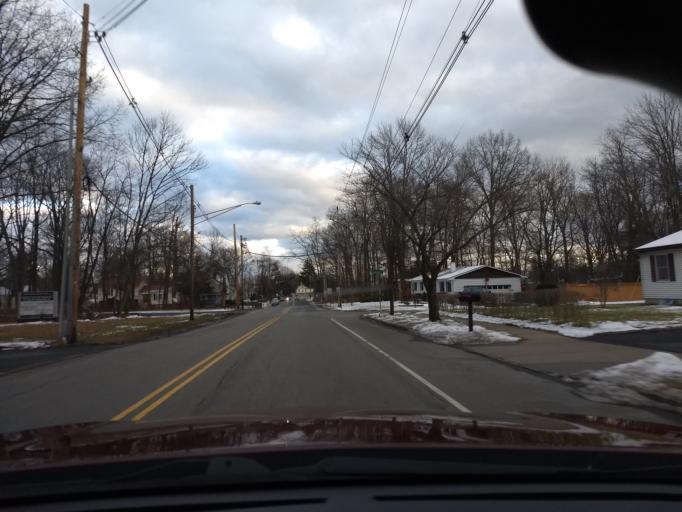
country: US
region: New Jersey
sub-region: Morris County
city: Morris Plains
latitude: 40.8100
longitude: -74.4753
